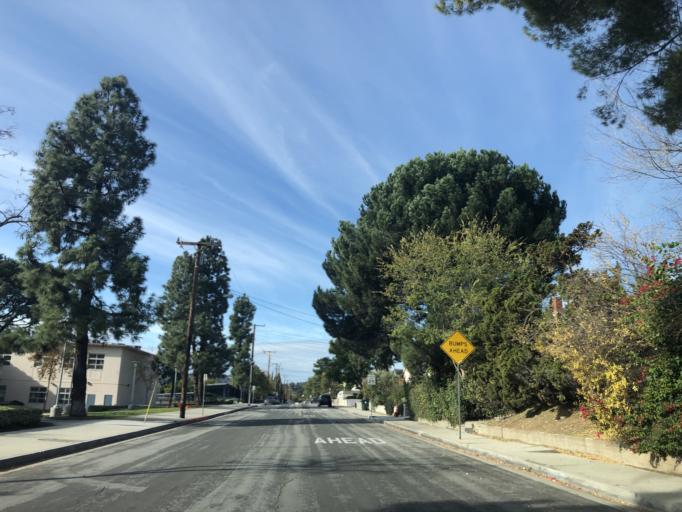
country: US
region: California
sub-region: Los Angeles County
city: La Crescenta-Montrose
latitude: 34.2237
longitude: -118.2422
